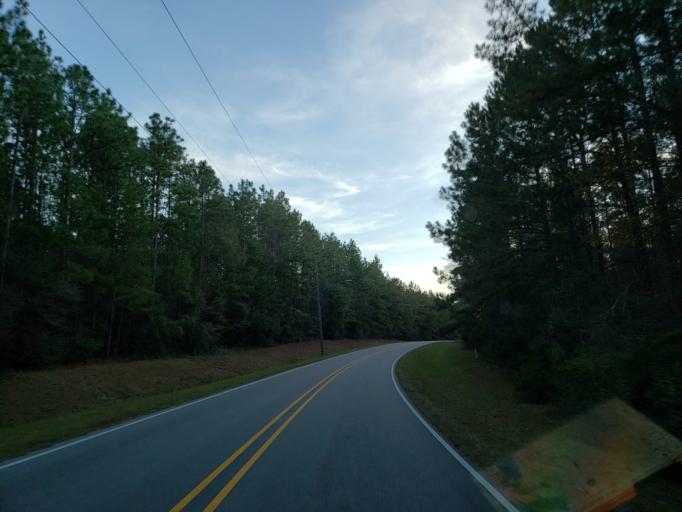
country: US
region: Mississippi
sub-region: Forrest County
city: Hattiesburg
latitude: 31.2693
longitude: -89.3092
